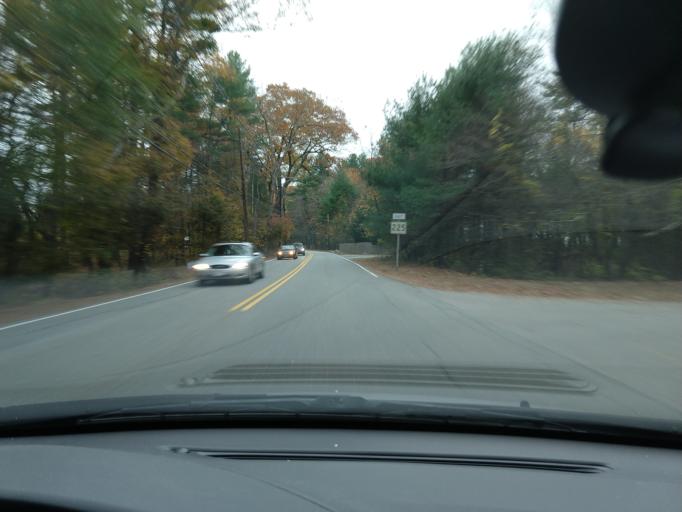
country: US
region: Massachusetts
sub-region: Middlesex County
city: Carlisle
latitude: 42.5208
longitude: -71.3308
